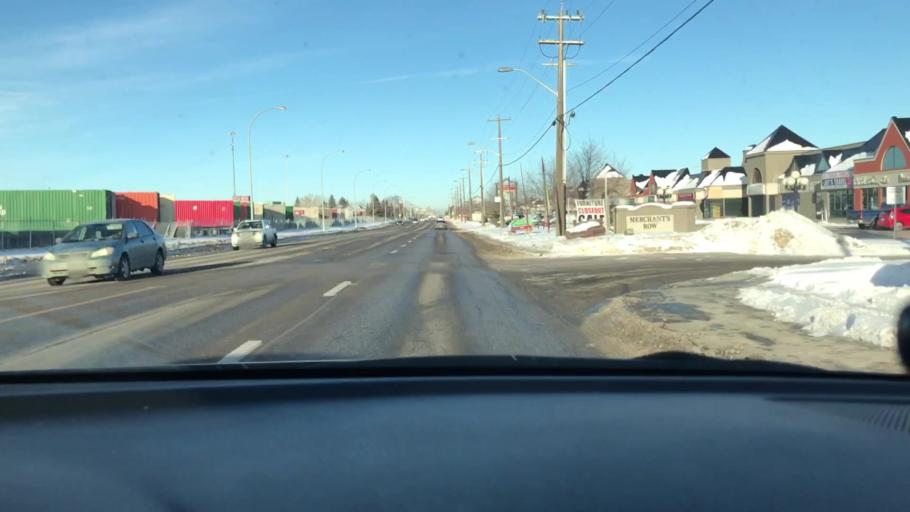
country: CA
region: Alberta
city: Edmonton
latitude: 53.4700
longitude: -113.4860
